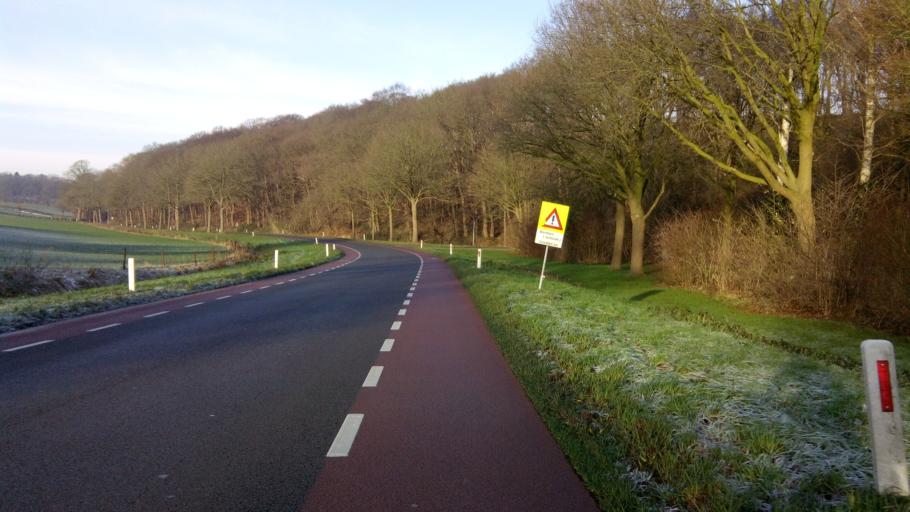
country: NL
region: Gelderland
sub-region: Gemeente Groesbeek
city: De Horst
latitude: 51.8093
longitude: 5.9571
